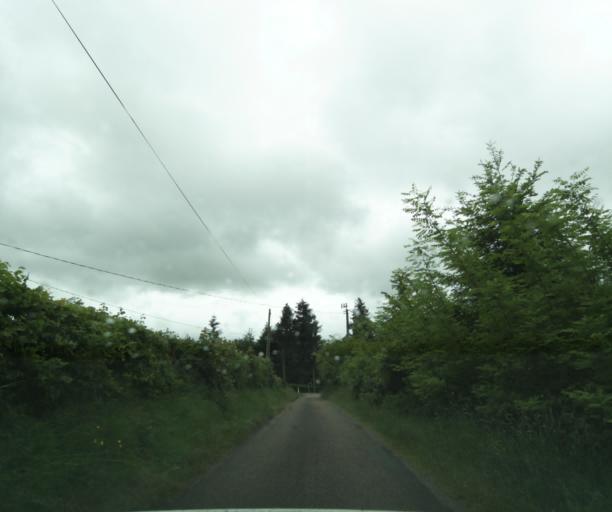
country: FR
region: Bourgogne
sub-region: Departement de Saone-et-Loire
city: Matour
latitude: 46.4265
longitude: 4.4387
